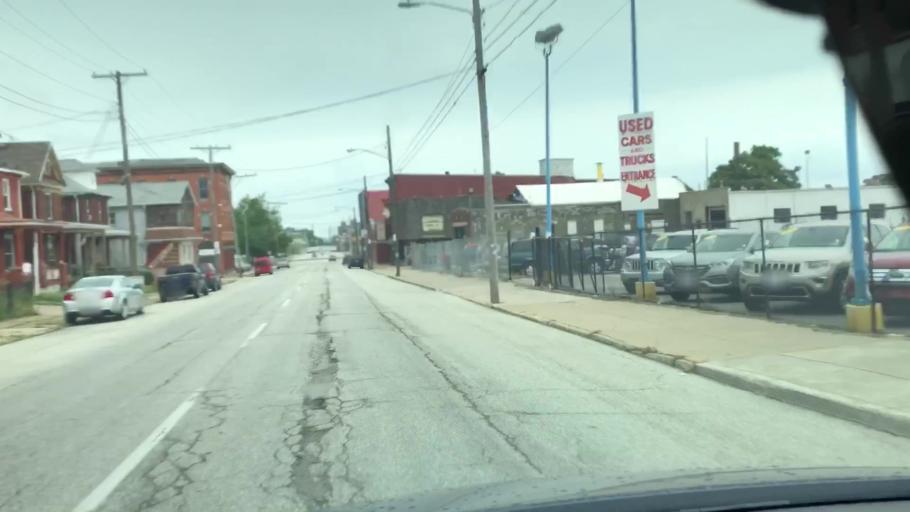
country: US
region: Pennsylvania
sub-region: Erie County
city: Erie
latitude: 42.1158
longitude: -80.0778
